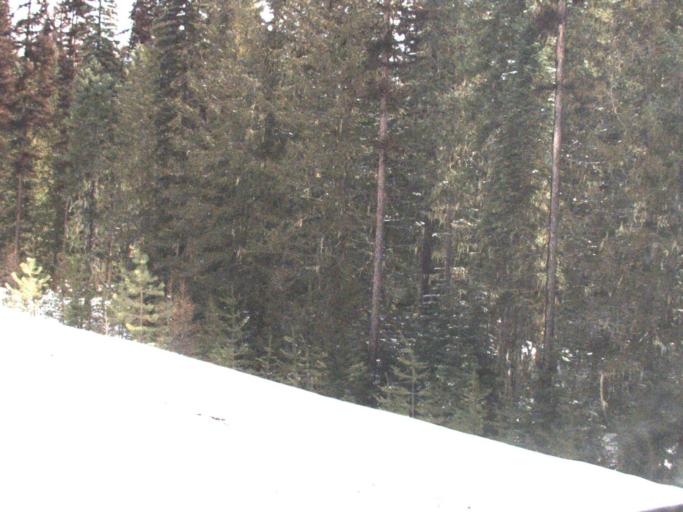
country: US
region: Washington
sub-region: Stevens County
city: Colville
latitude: 48.6342
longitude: -117.5359
